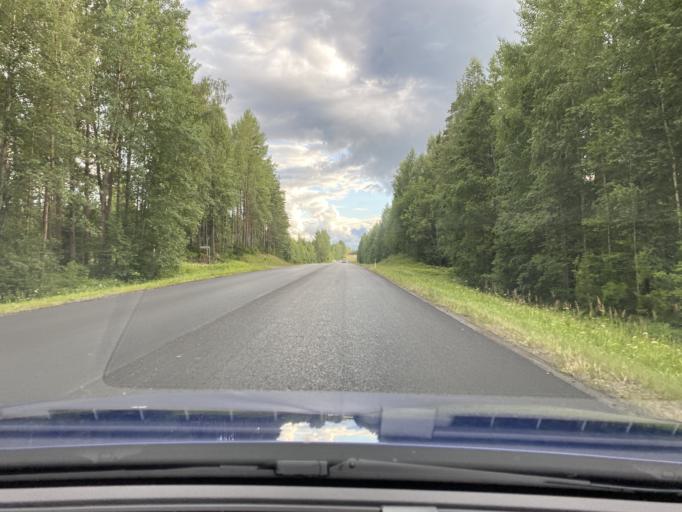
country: FI
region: Haeme
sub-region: Haemeenlinna
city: Renko
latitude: 60.9191
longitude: 24.3314
